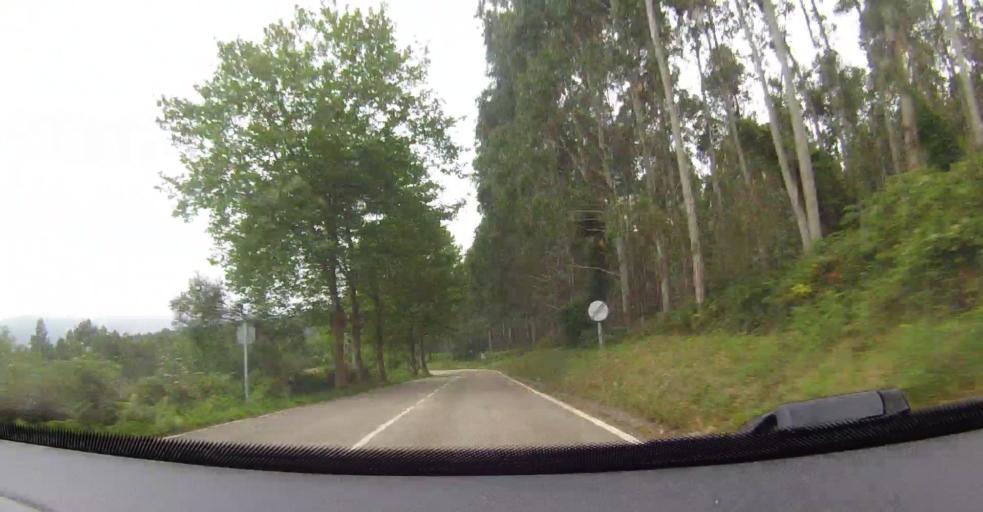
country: ES
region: Basque Country
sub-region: Bizkaia
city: Balmaseda
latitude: 43.2368
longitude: -3.2931
